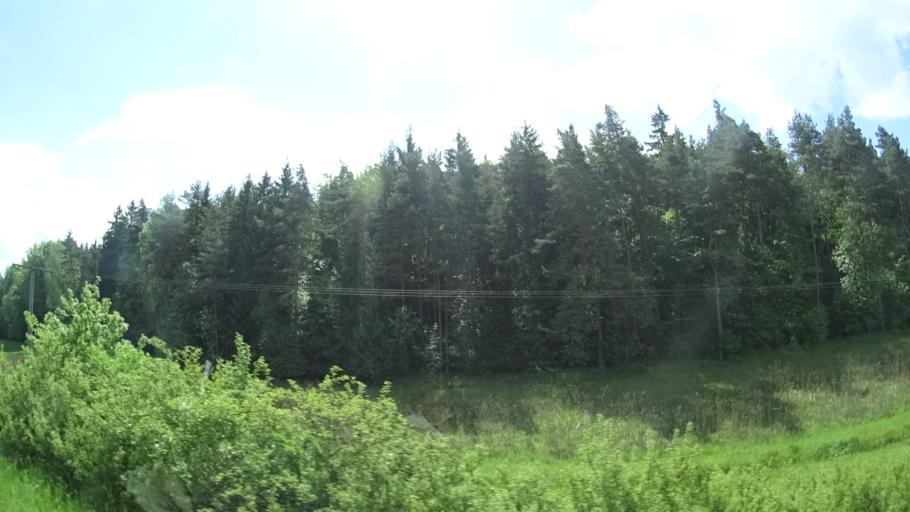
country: DE
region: Bavaria
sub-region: Regierungsbezirk Unterfranken
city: Ostheim vor der Rhon
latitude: 50.4225
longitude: 10.2356
